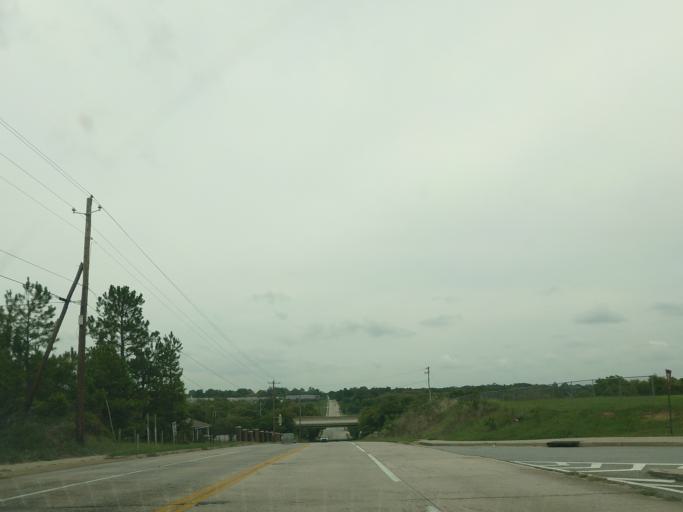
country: US
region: Georgia
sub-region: Bibb County
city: Macon
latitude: 32.8201
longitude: -83.6579
